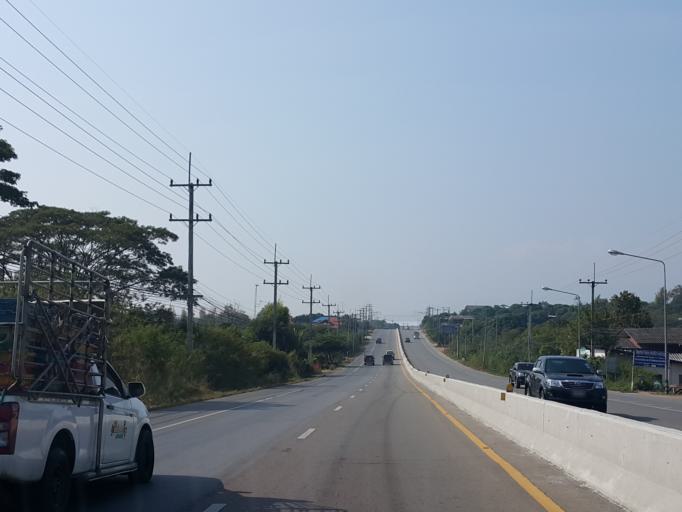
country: TH
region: Chiang Mai
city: Doi Lo
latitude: 18.4628
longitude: 98.7806
